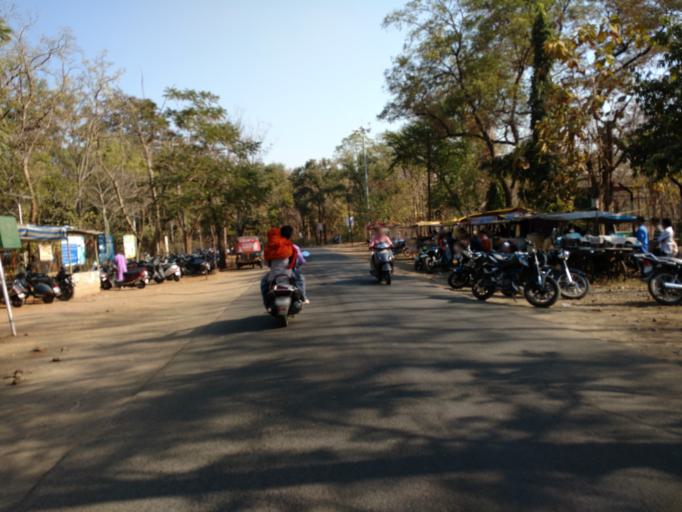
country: IN
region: Maharashtra
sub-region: Nagpur Division
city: Nagpur
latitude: 21.1678
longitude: 79.0641
